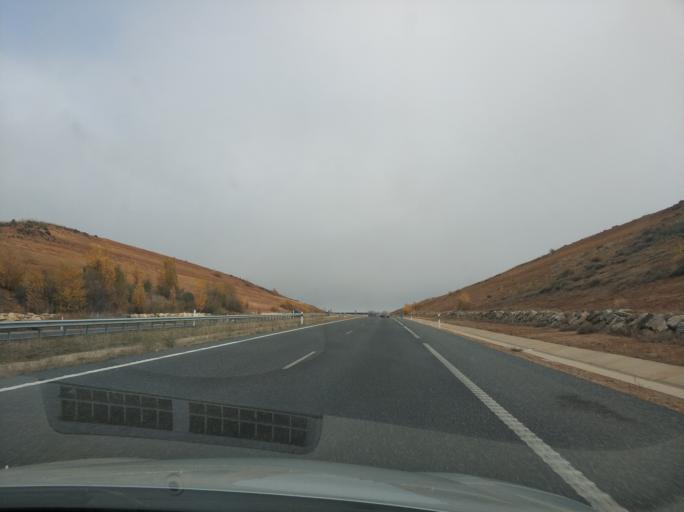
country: ES
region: Castille and Leon
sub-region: Provincia de Leon
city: Valdefresno
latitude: 42.5635
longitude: -5.5311
